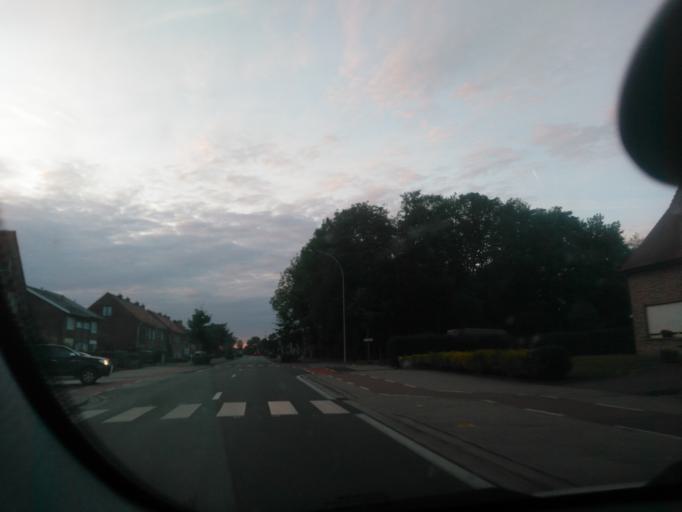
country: BE
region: Flanders
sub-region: Provincie Oost-Vlaanderen
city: Sint-Gillis-Waas
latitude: 51.2594
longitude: 4.1883
